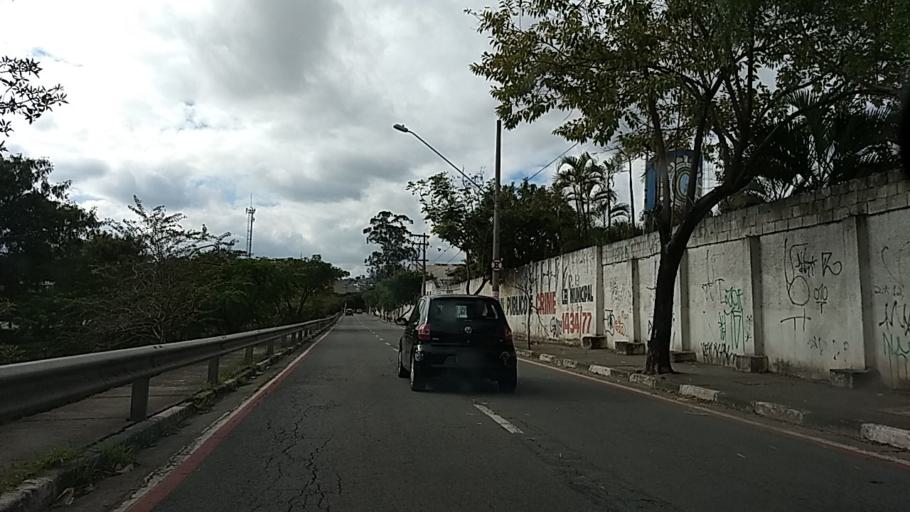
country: BR
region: Sao Paulo
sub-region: Osasco
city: Osasco
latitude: -23.5183
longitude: -46.7758
